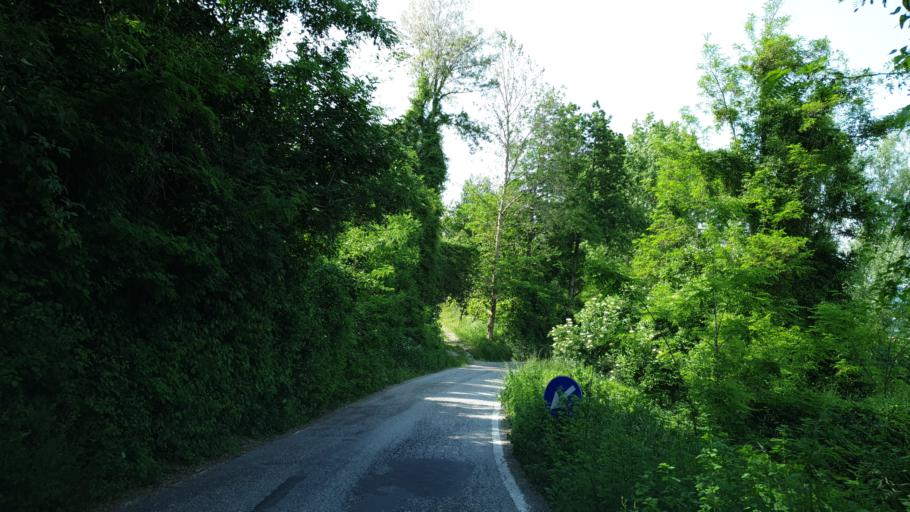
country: IT
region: Emilia-Romagna
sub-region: Forli-Cesena
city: Sarsina
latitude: 43.9117
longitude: 12.1755
